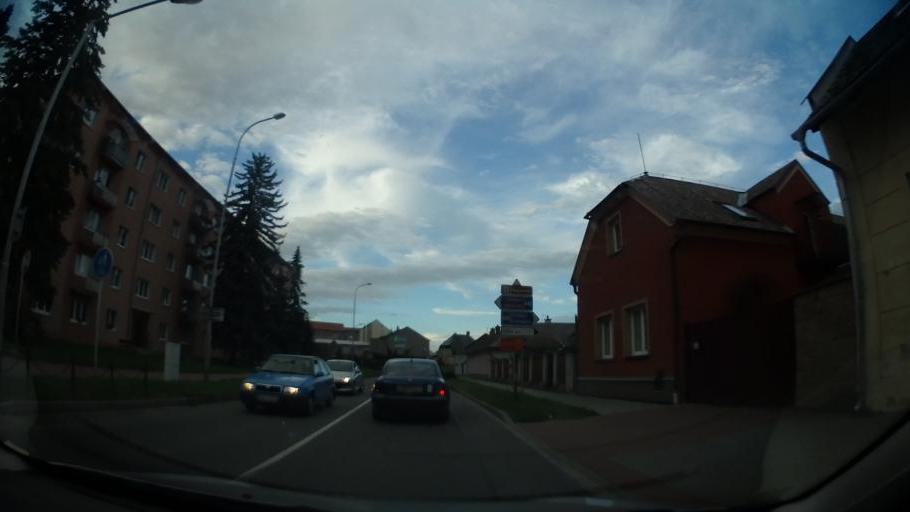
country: CZ
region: Olomoucky
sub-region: Okres Olomouc
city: Unicov
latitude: 49.7679
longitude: 17.1182
